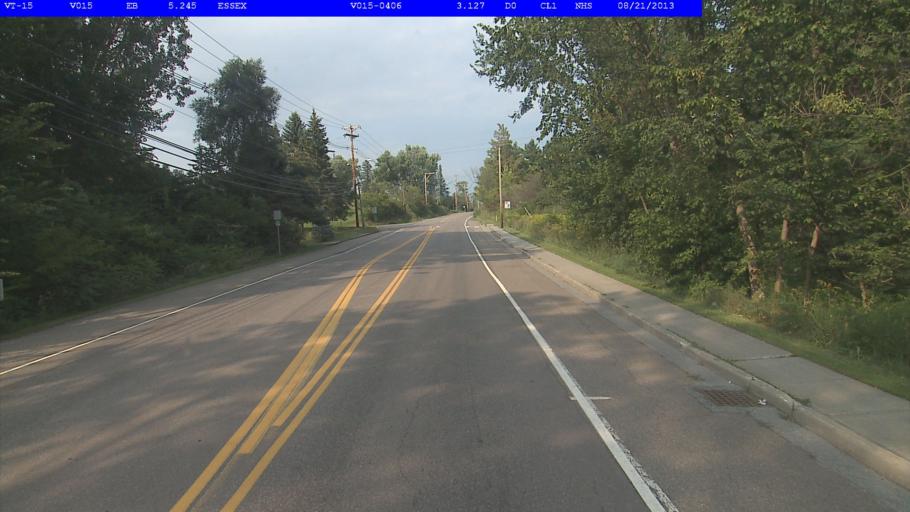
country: US
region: Vermont
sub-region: Chittenden County
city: Essex Junction
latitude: 44.4995
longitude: -73.0980
